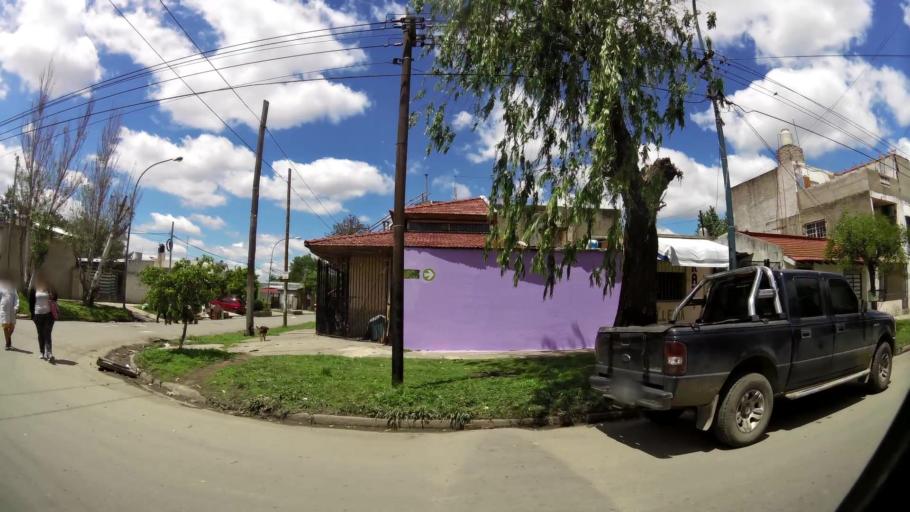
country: AR
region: Buenos Aires
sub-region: Partido de Lanus
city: Lanus
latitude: -34.7028
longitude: -58.4347
